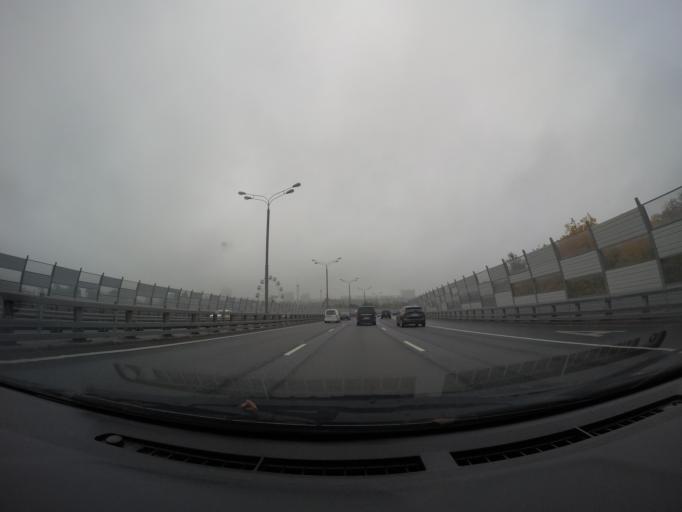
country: RU
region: Moscow
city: Shchukino
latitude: 55.7736
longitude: 37.4373
